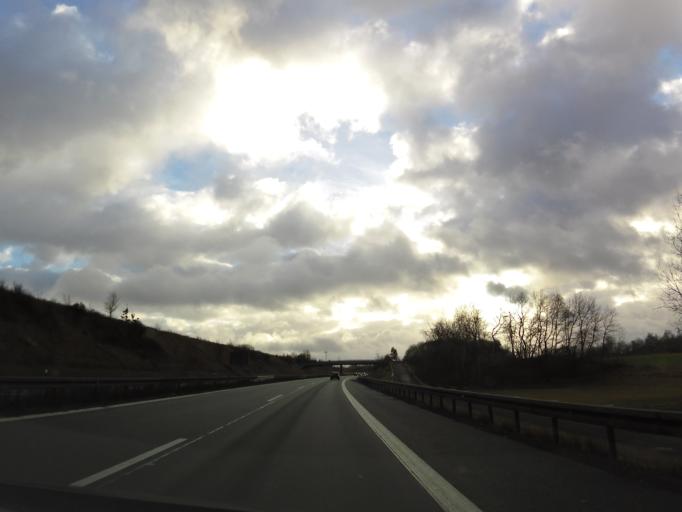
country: DE
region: Bavaria
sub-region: Upper Franconia
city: Thierstein
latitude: 50.1110
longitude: 12.0964
